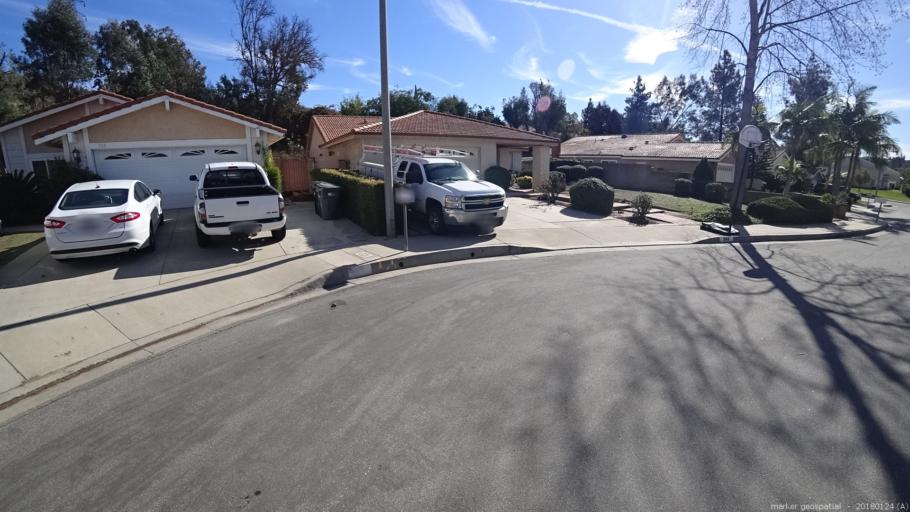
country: US
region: California
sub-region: Los Angeles County
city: Diamond Bar
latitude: 34.0052
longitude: -117.8050
